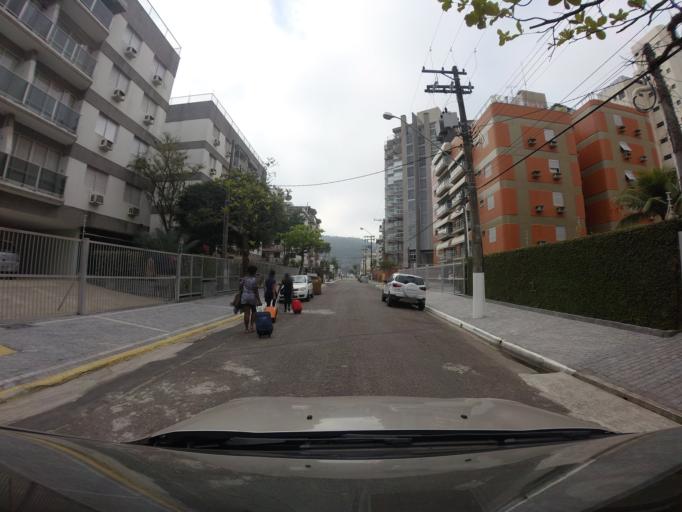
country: BR
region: Sao Paulo
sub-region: Guaruja
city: Guaruja
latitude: -23.9839
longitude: -46.2331
